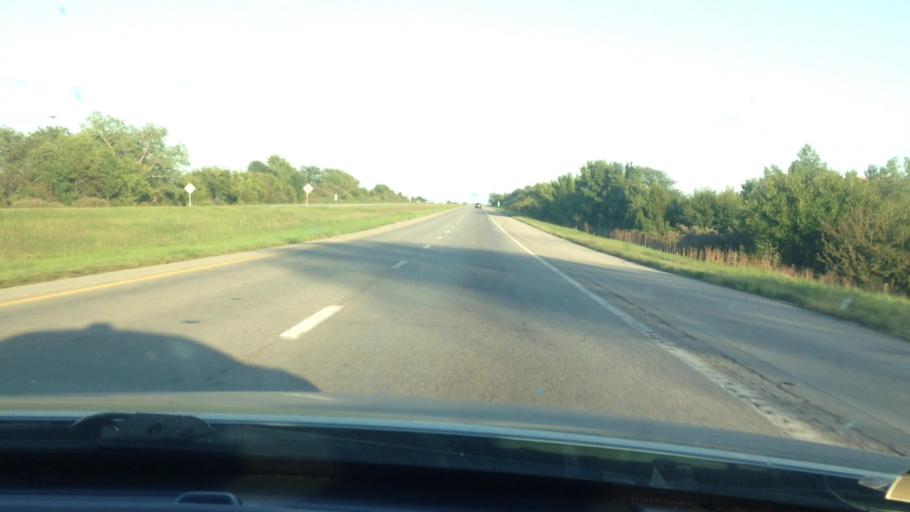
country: US
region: Missouri
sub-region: Platte County
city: Weatherby Lake
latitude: 39.3182
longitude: -94.6916
